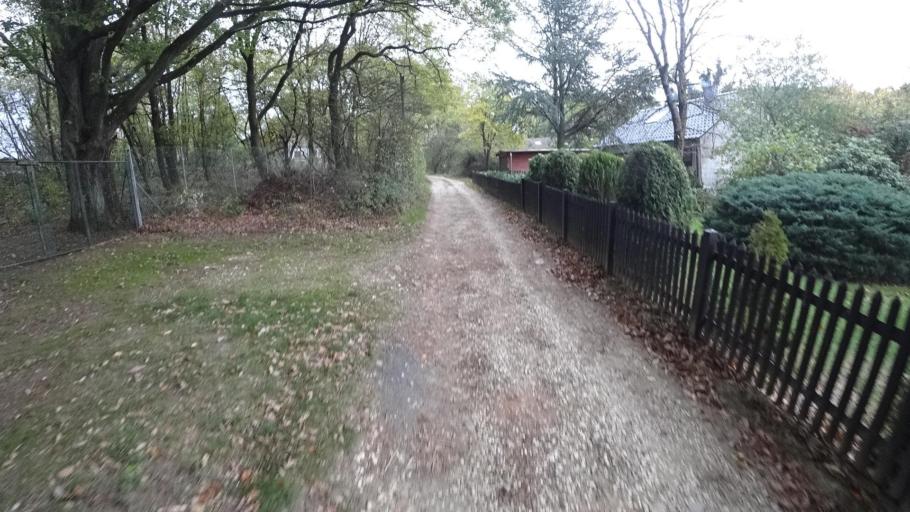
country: DE
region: Rheinland-Pfalz
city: Berg
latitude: 50.5469
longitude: 6.9260
